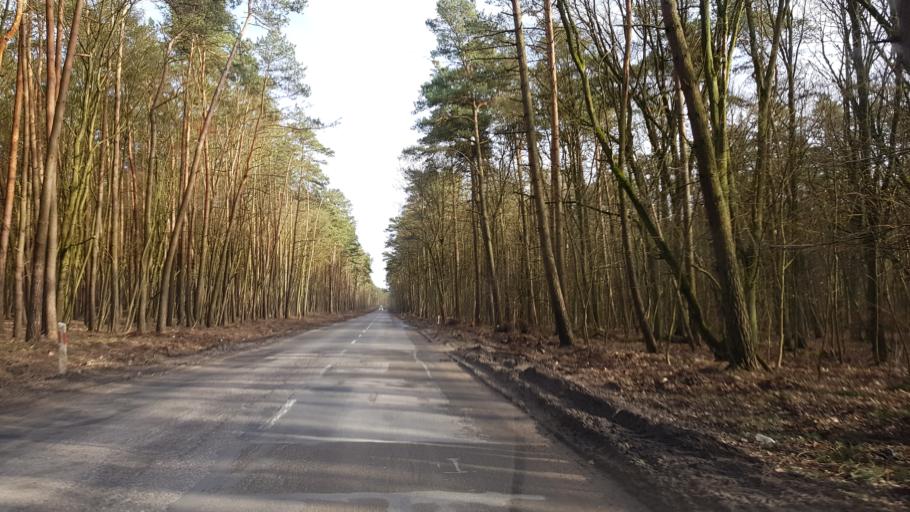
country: PL
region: West Pomeranian Voivodeship
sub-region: Powiat policki
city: Dobra
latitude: 53.4761
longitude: 14.4623
